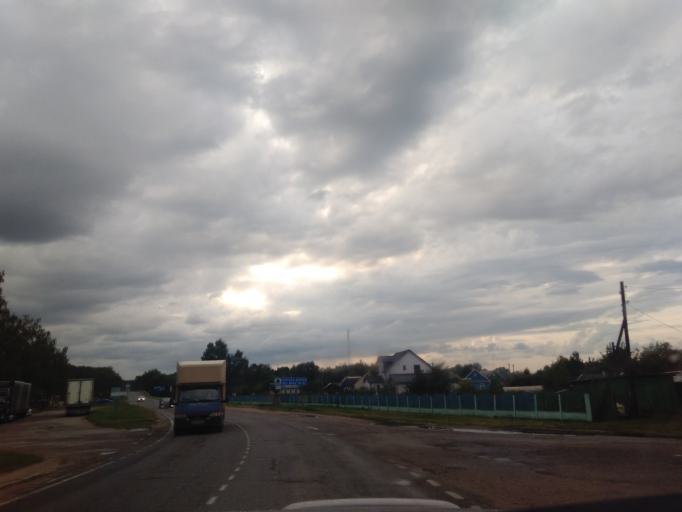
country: BY
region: Minsk
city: Enyerhyetykaw
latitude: 53.5879
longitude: 27.0520
